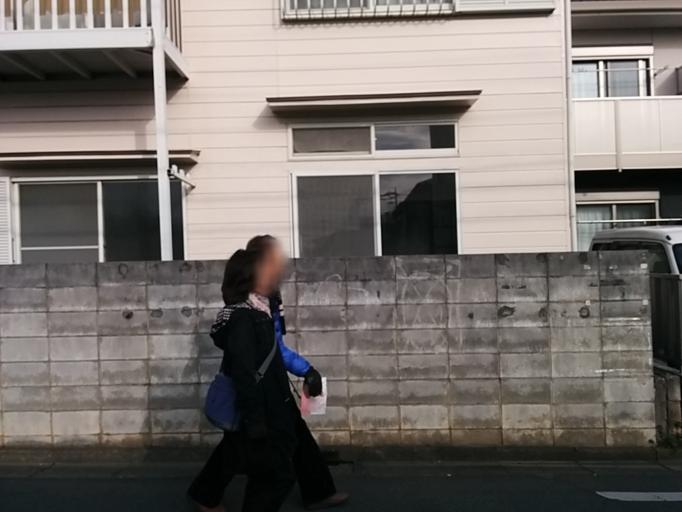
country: JP
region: Saitama
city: Kawagoe
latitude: 35.9048
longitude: 139.4897
